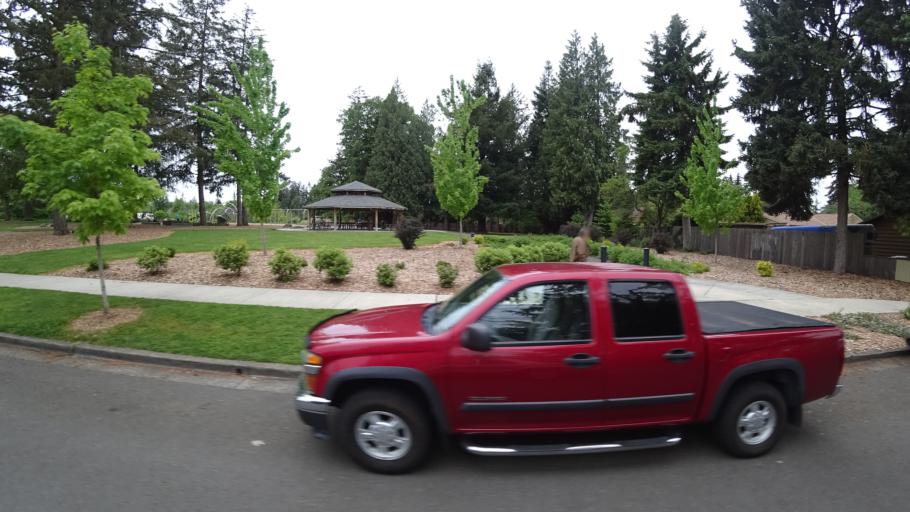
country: US
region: Oregon
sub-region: Washington County
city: Beaverton
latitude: 45.4804
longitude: -122.8119
